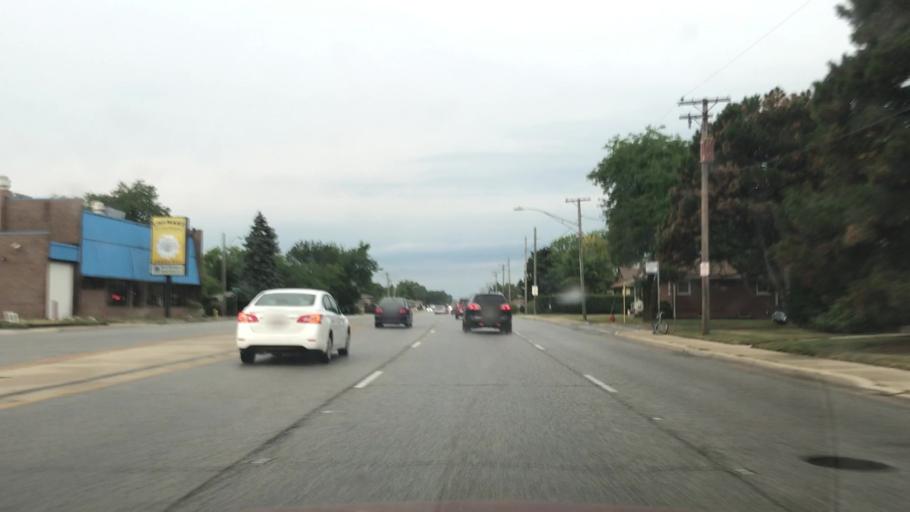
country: US
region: Illinois
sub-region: Cook County
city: Niles
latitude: 42.0408
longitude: -87.8101
